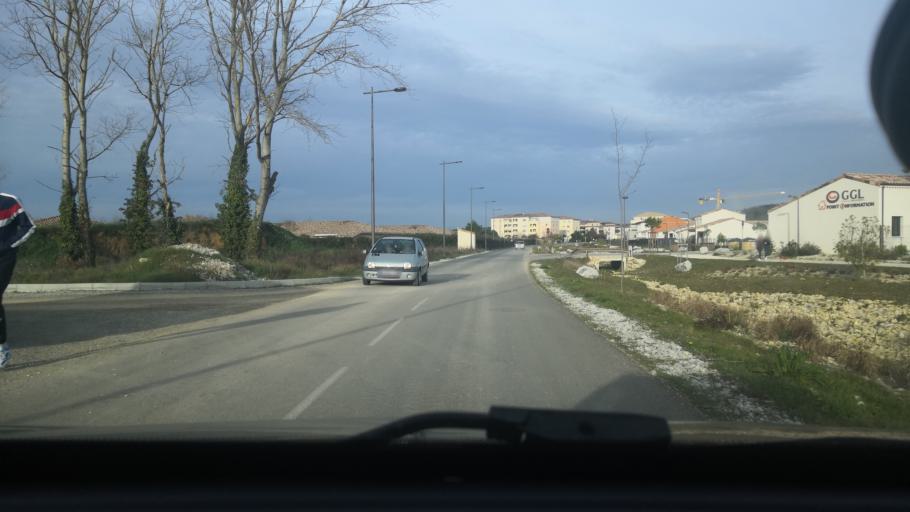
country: FR
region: Rhone-Alpes
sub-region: Departement de la Drome
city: Montelimar
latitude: 44.5326
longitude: 4.7621
